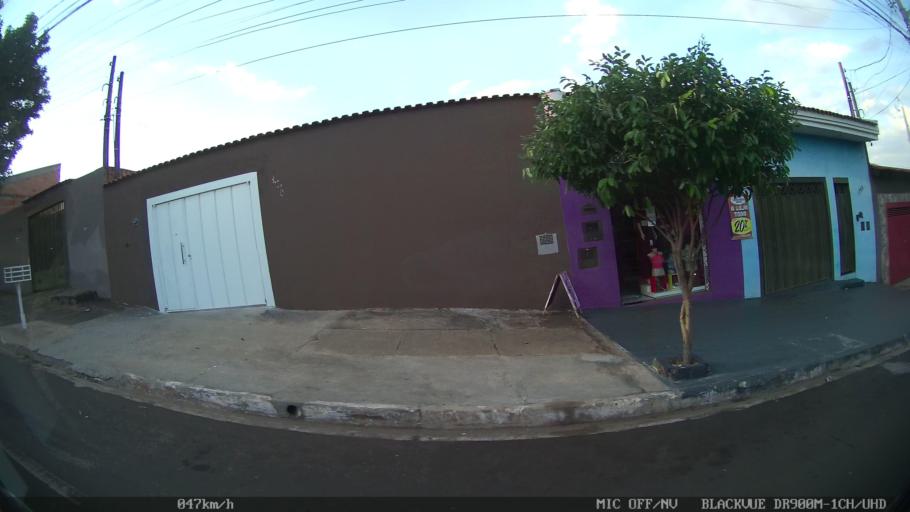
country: BR
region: Sao Paulo
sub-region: Ribeirao Preto
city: Ribeirao Preto
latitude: -21.1502
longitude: -47.8461
